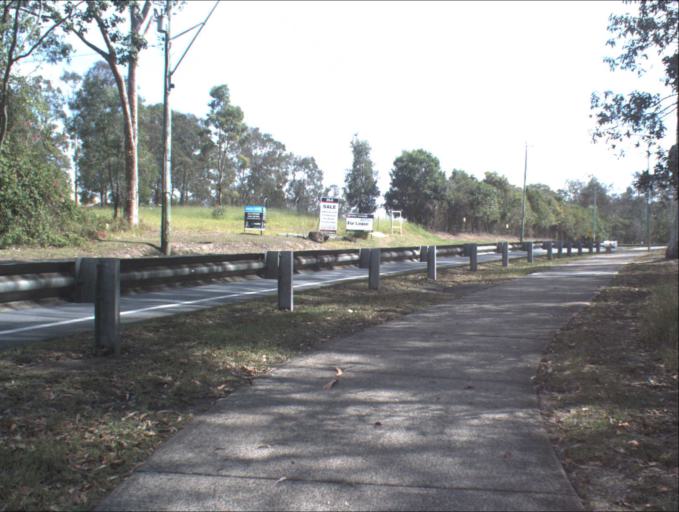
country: AU
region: Queensland
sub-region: Logan
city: Slacks Creek
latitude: -27.6555
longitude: 153.1407
